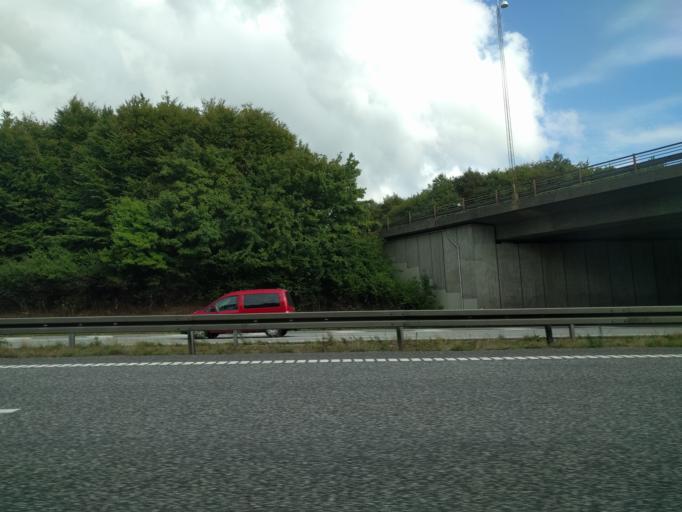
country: DK
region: South Denmark
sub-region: Vejle Kommune
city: Vejle
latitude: 55.7244
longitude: 9.5758
